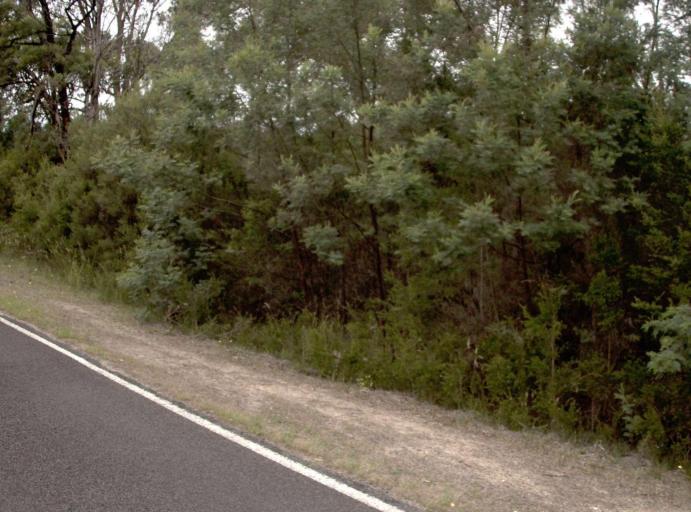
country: AU
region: Victoria
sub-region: Latrobe
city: Traralgon
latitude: -38.5037
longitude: 146.8378
